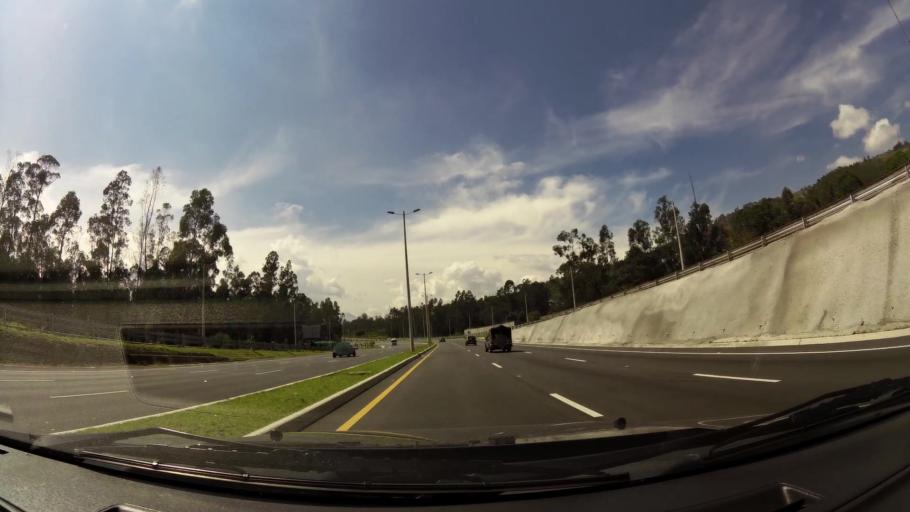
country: EC
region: Pichincha
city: Quito
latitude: -0.2243
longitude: -78.4127
